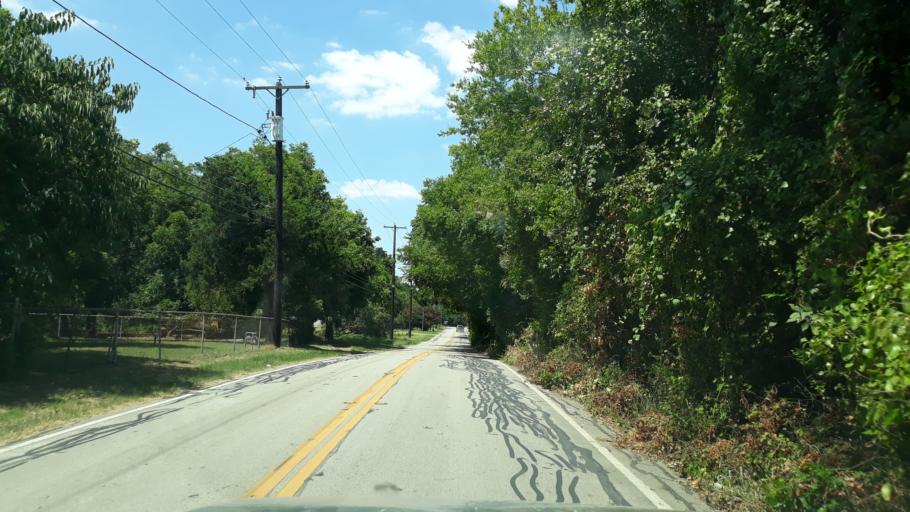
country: US
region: Texas
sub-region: Tarrant County
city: Euless
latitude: 32.8130
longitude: -97.0203
